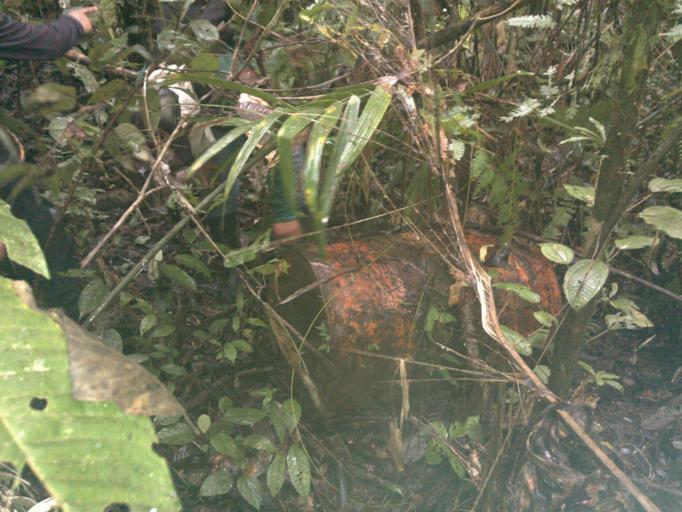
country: EC
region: Orellana
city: Boca Suno
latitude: -1.1385
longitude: -76.8122
